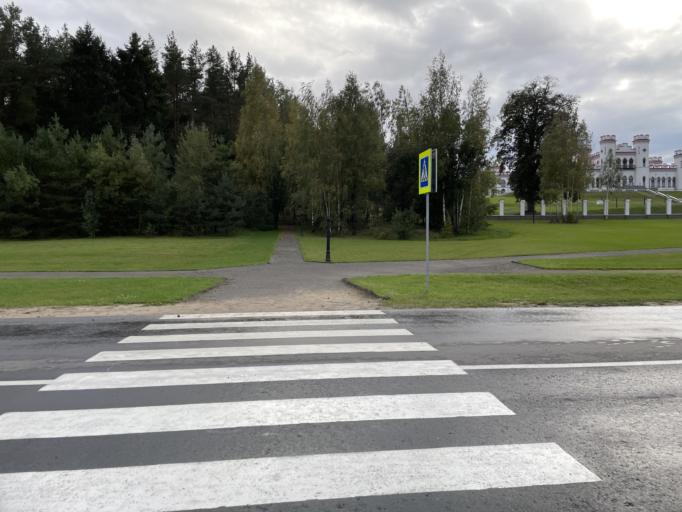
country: BY
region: Brest
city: Kosava
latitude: 52.7663
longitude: 25.1250
